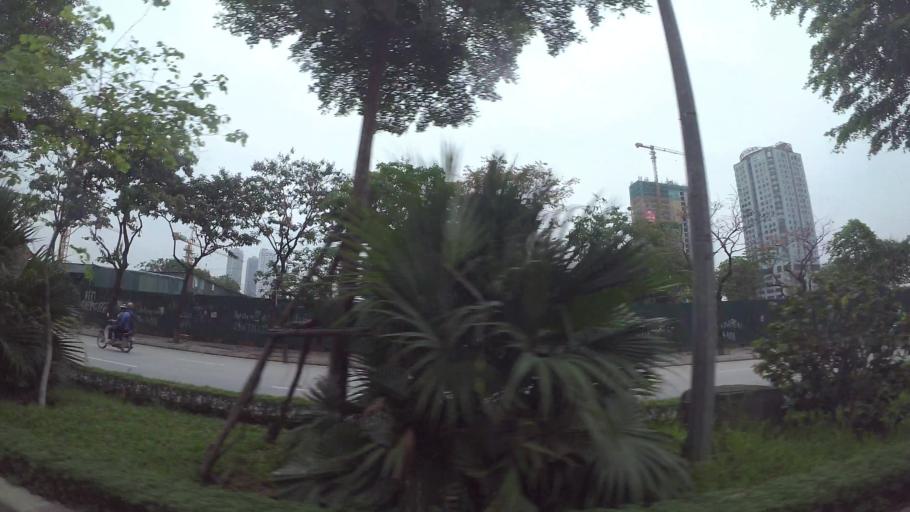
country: VN
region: Ha Noi
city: Cau Giay
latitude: 21.0252
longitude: 105.7892
